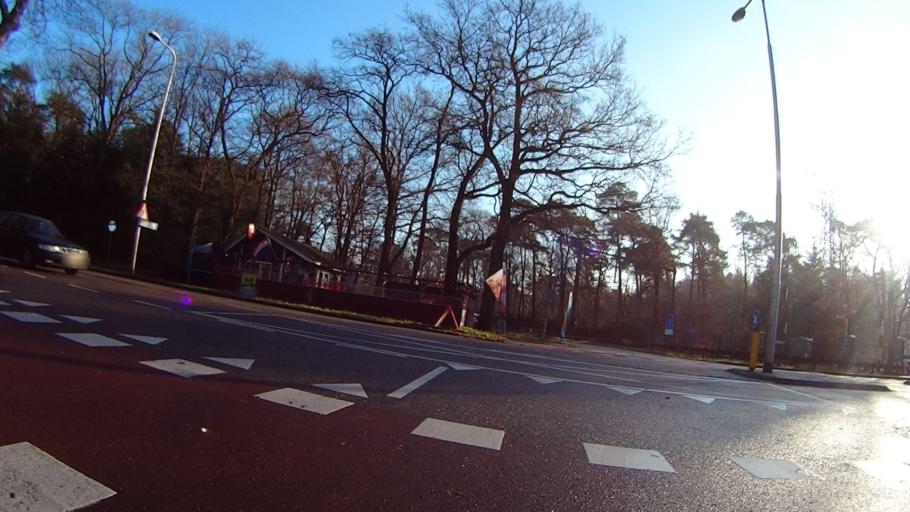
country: NL
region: Utrecht
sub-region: Gemeente Soest
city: Soest
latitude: 52.1453
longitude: 5.3002
